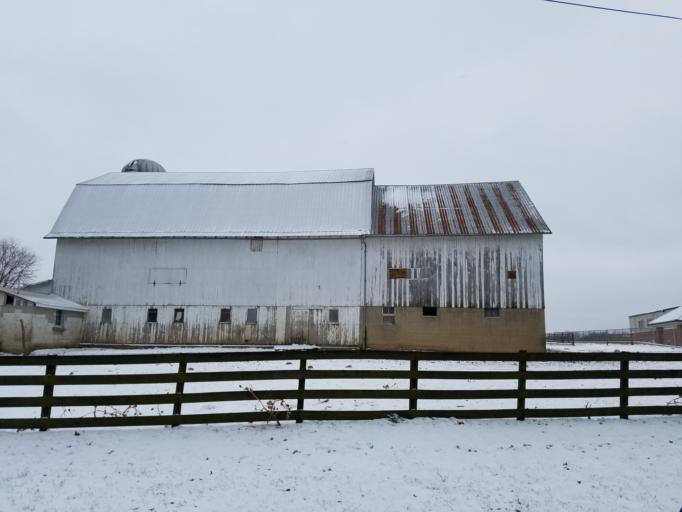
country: US
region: Ohio
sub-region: Knox County
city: Fredericktown
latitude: 40.5430
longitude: -82.6235
